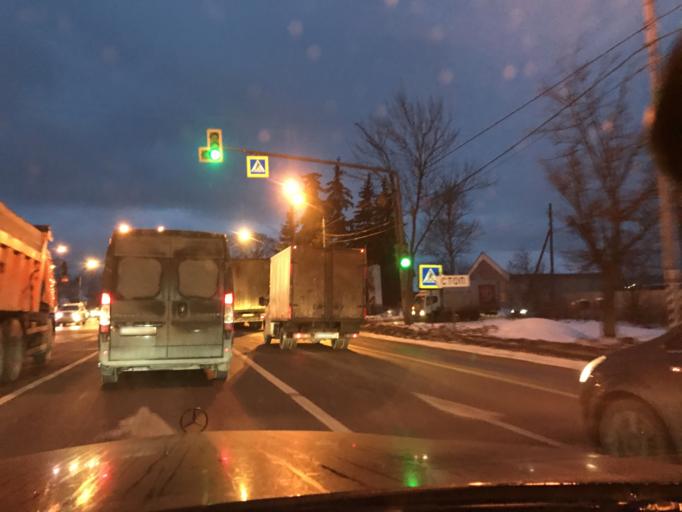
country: RU
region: Moskovskaya
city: Malaya Dubna
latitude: 55.8764
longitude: 38.9630
